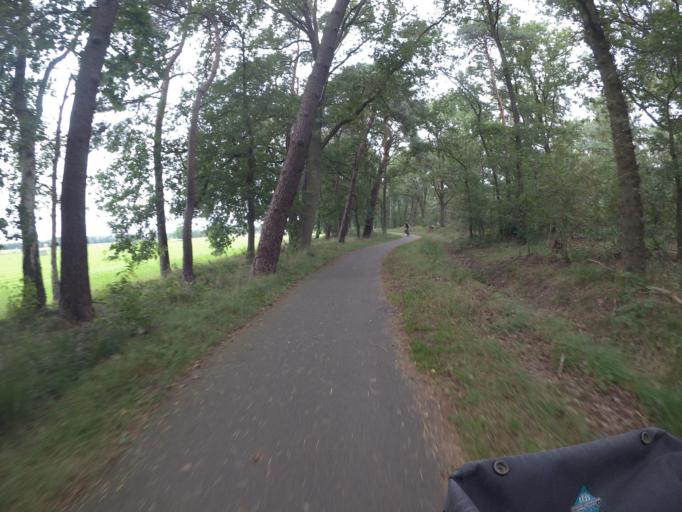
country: NL
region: North Brabant
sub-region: Gemeente Valkenswaard
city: Valkenswaard
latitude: 51.3316
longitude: 5.4438
